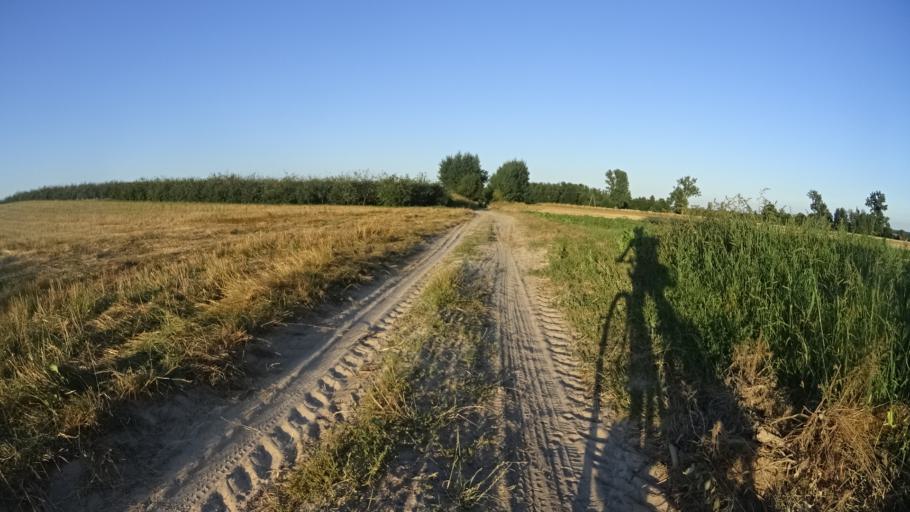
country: PL
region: Masovian Voivodeship
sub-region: Powiat bialobrzeski
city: Wysmierzyce
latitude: 51.6613
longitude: 20.8263
